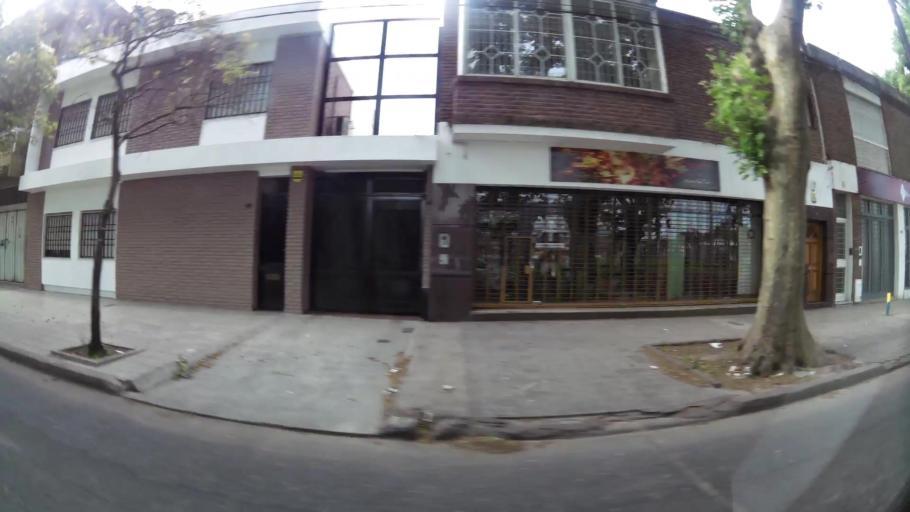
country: AR
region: Santa Fe
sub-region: Departamento de Rosario
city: Rosario
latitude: -32.9265
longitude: -60.6725
